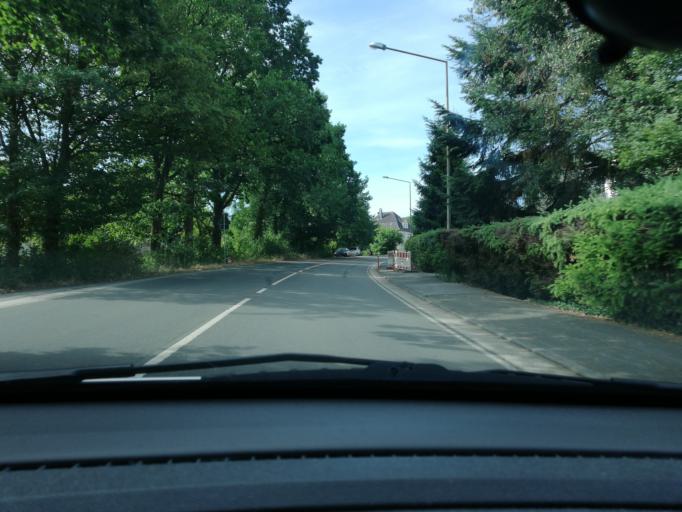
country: DE
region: North Rhine-Westphalia
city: Gevelsberg
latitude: 51.3320
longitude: 7.3372
